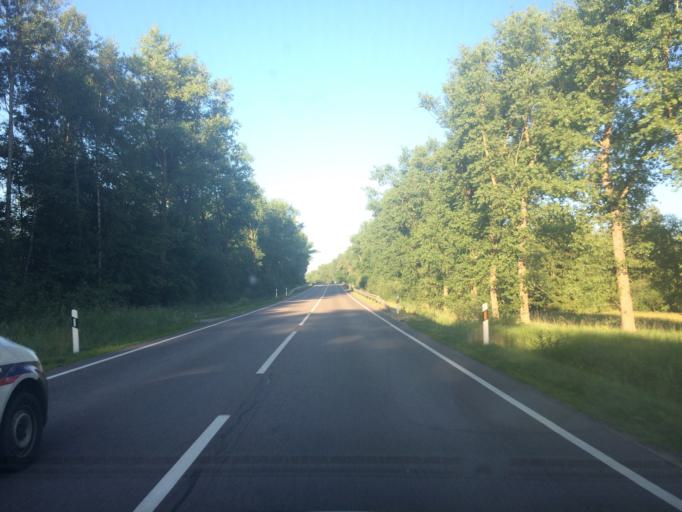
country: LT
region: Utenos apskritis
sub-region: Anyksciai
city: Anyksciai
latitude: 55.4260
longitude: 25.2321
